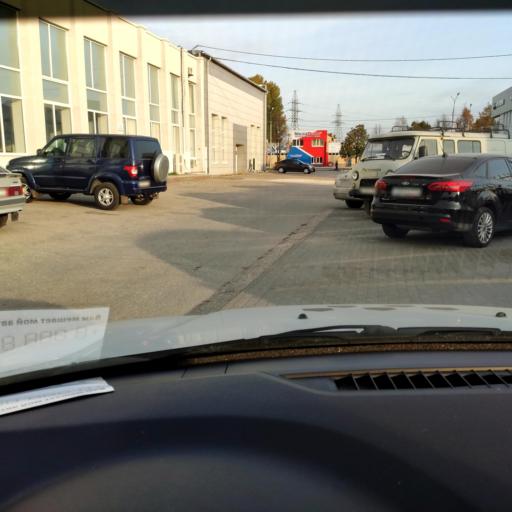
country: RU
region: Samara
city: Tol'yatti
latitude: 53.5394
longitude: 49.4117
